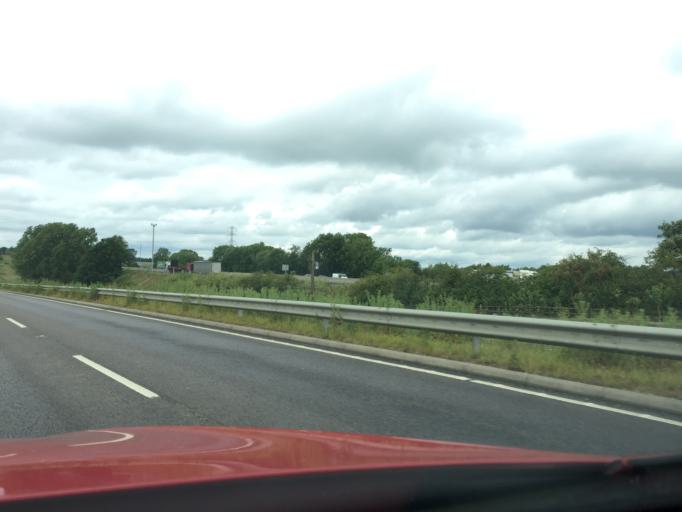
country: GB
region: England
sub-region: Northamptonshire
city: Bugbrooke
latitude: 52.2359
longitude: -1.0392
